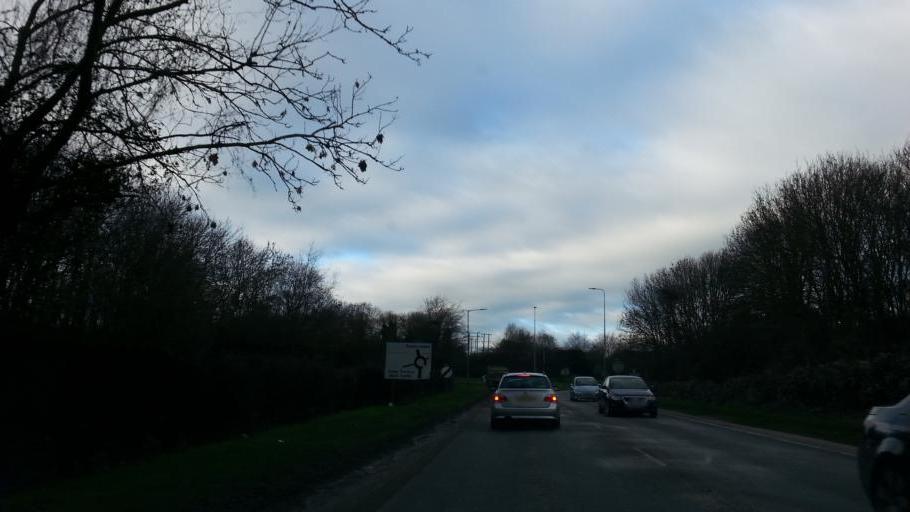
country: GB
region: England
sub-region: Suffolk
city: Bury St Edmunds
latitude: 52.2611
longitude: 0.7268
